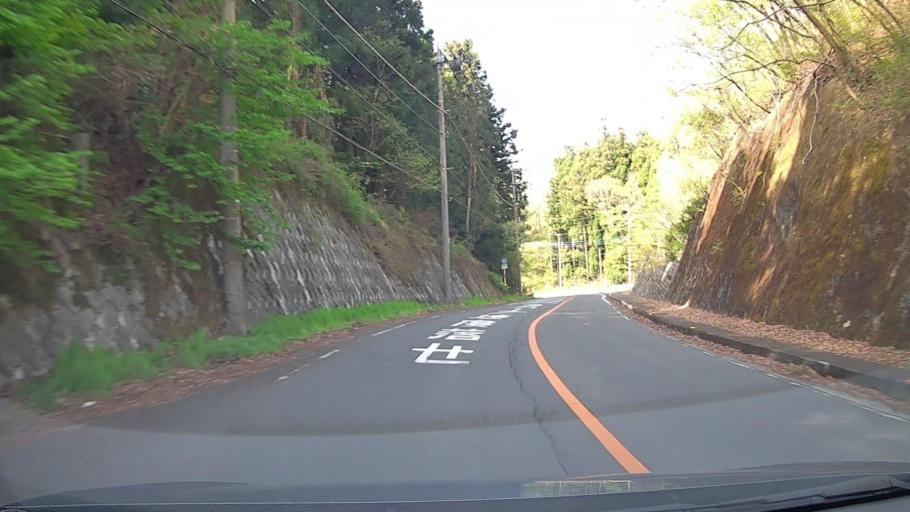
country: JP
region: Saitama
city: Chichibu
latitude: 36.0334
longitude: 139.1276
